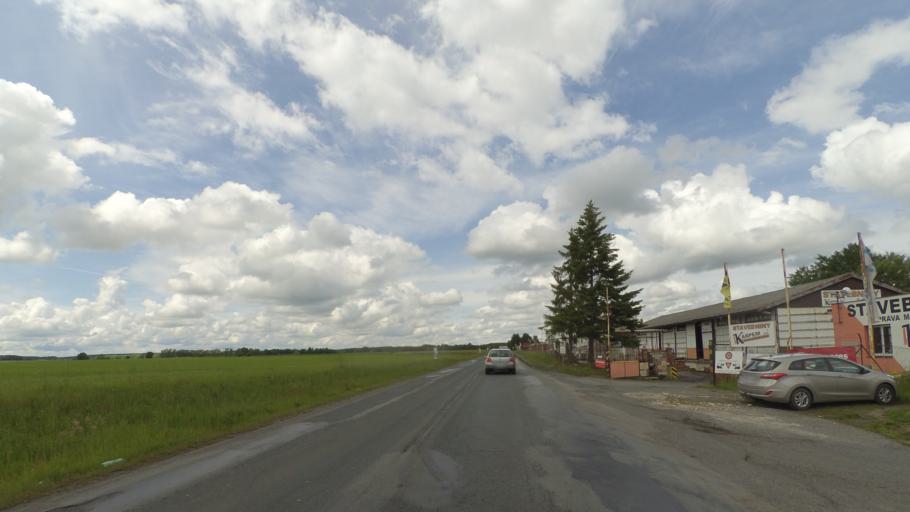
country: CZ
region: Plzensky
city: Bor
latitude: 49.7200
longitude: 12.7785
